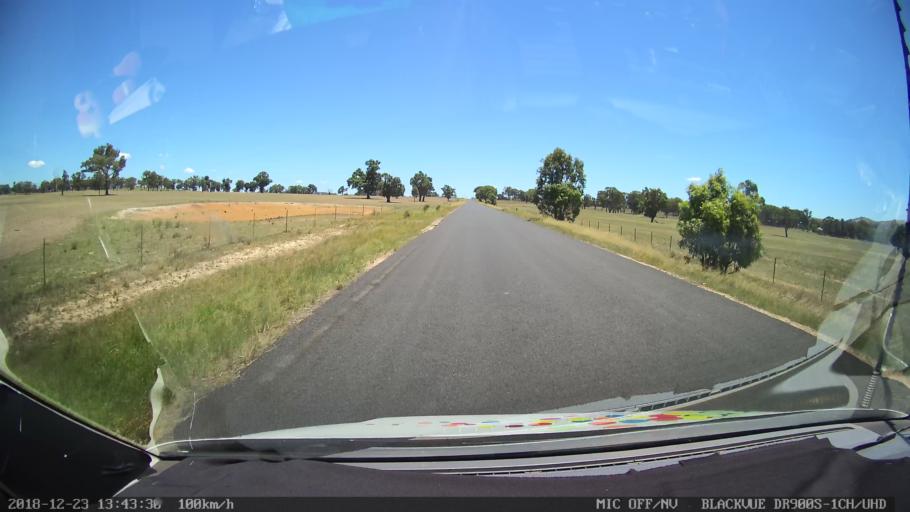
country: AU
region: New South Wales
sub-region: Tamworth Municipality
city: Manilla
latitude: -30.4866
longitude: 151.1489
